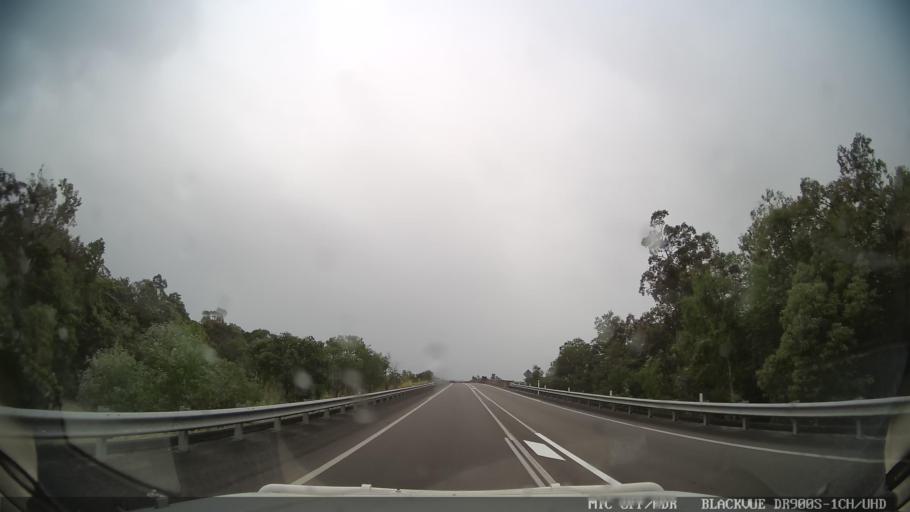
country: AU
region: Queensland
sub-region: Hinchinbrook
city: Ingham
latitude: -18.5121
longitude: 146.1879
